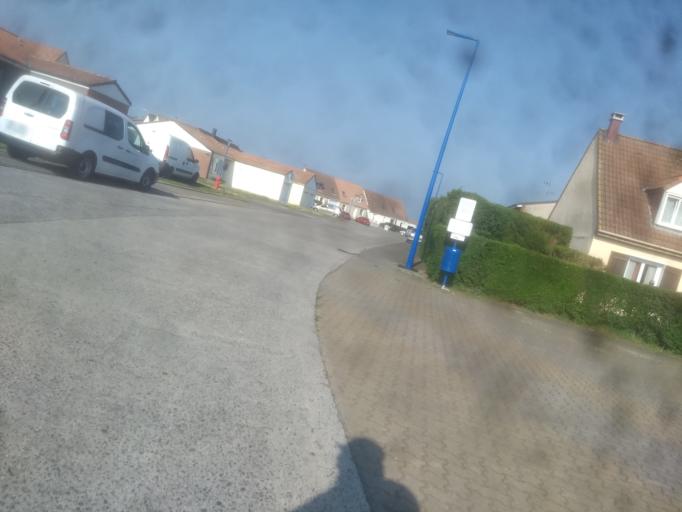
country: FR
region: Nord-Pas-de-Calais
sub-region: Departement du Pas-de-Calais
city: Beaurains
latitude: 50.2584
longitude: 2.7912
